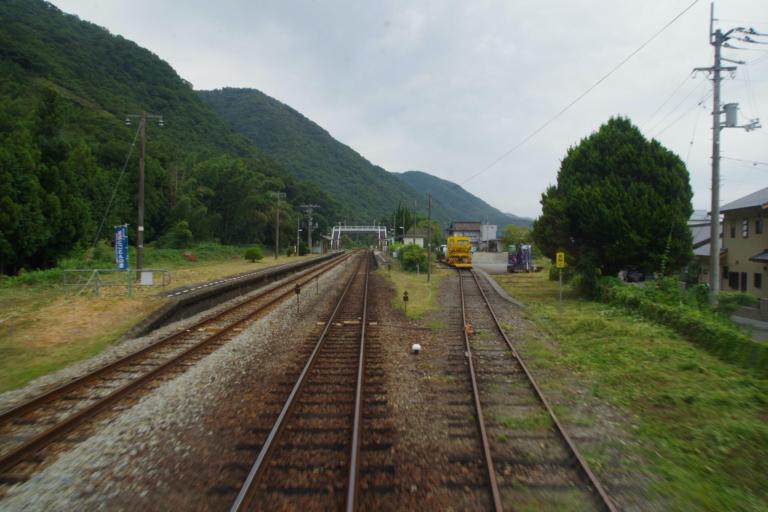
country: JP
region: Tokushima
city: Ikedacho
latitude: 34.0401
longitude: 133.8481
